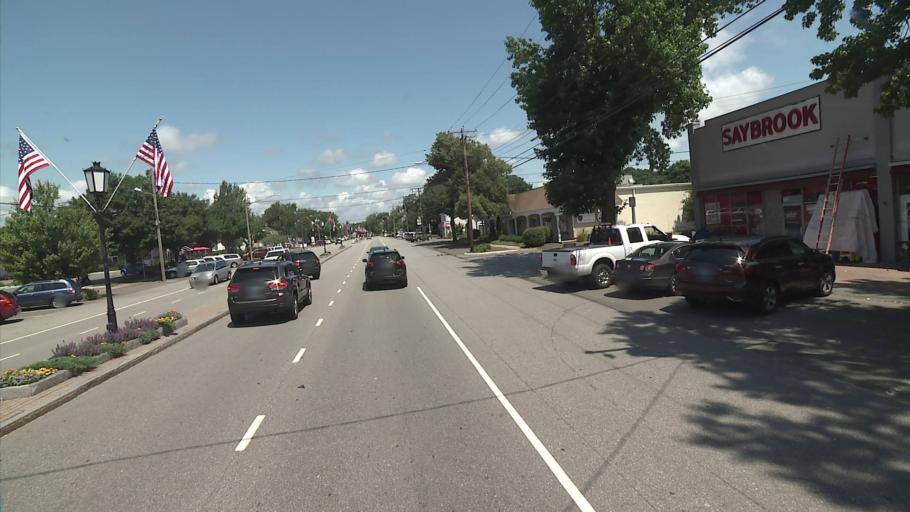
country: US
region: Connecticut
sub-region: Middlesex County
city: Old Saybrook
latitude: 41.2940
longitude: -72.3765
